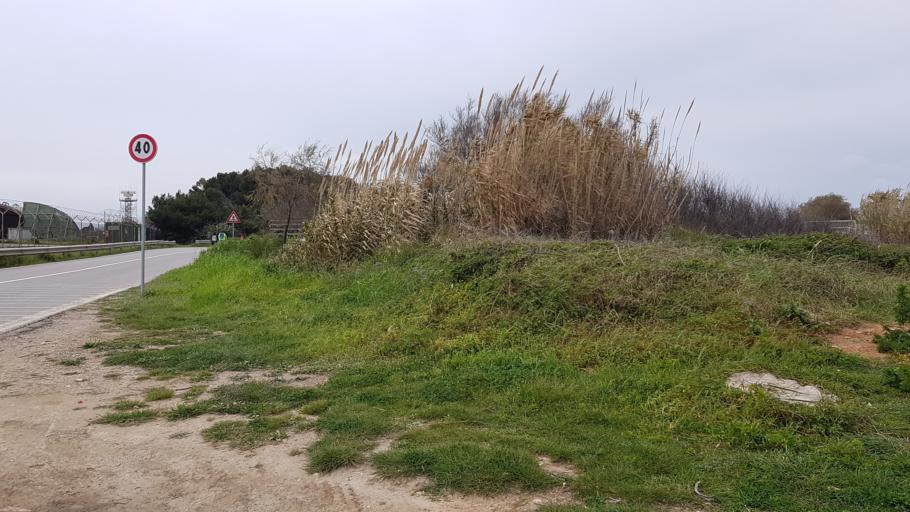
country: IT
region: Apulia
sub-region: Provincia di Brindisi
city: Materdomini
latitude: 40.6638
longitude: 17.9532
